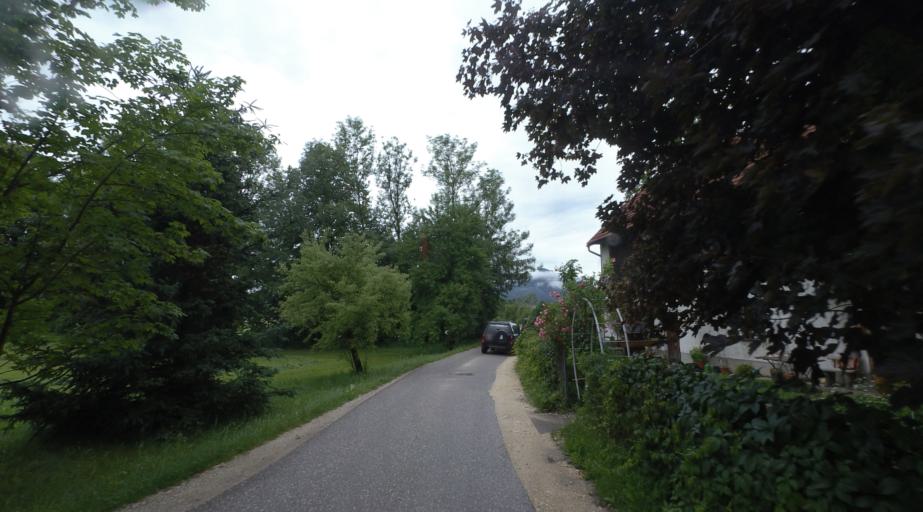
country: AT
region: Upper Austria
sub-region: Politischer Bezirk Kirchdorf an der Krems
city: Gruenburg
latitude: 47.8923
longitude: 14.2671
